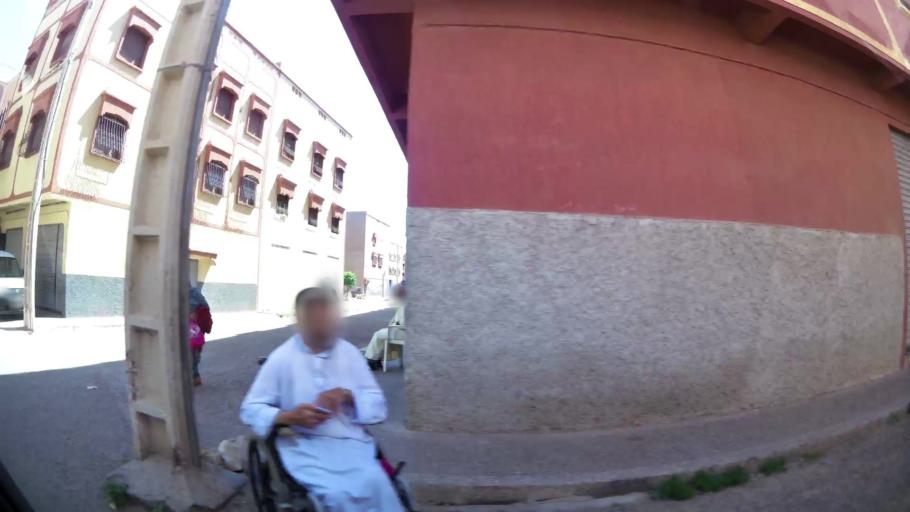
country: MA
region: Souss-Massa-Draa
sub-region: Inezgane-Ait Mellou
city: Inezgane
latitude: 30.3338
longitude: -9.5053
